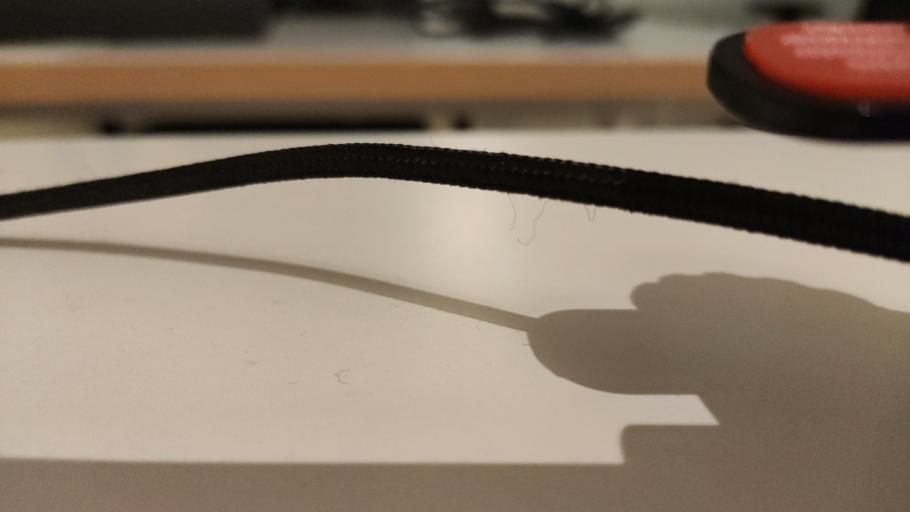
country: RU
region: Moskovskaya
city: Il'inskiy Pogost
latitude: 55.4981
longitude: 38.8740
